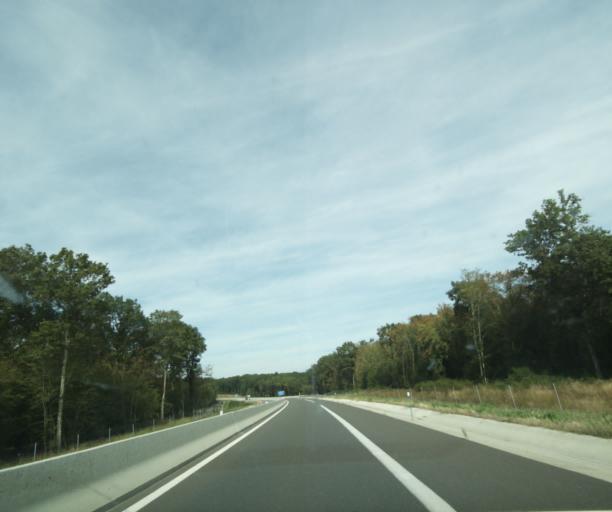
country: FR
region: Auvergne
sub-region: Departement de l'Allier
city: Vendat
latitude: 46.1281
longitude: 3.3627
